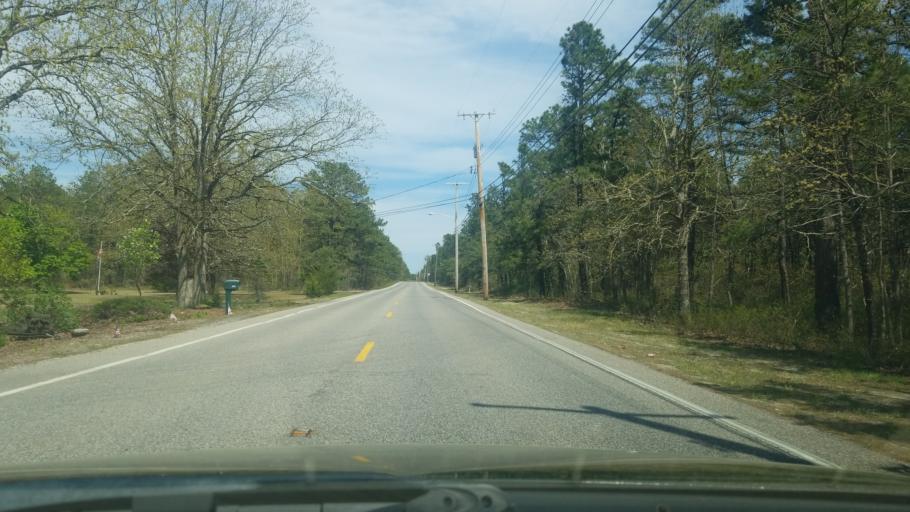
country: US
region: New Jersey
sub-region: Ocean County
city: Lakehurst
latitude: 40.0039
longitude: -74.3546
